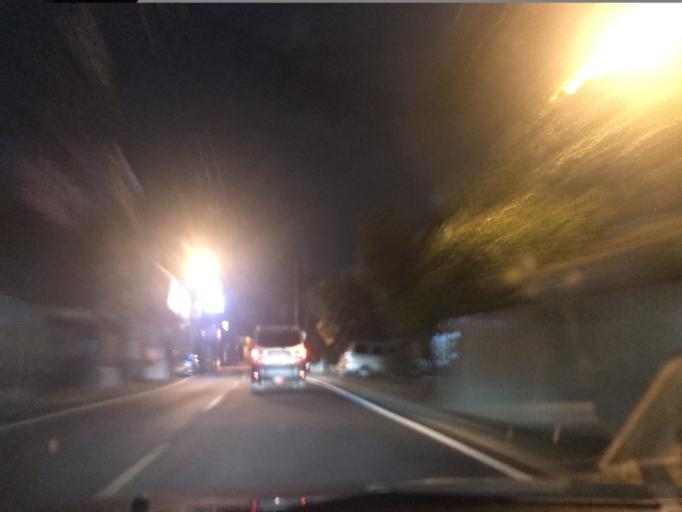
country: TW
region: Taiwan
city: Daxi
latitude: 24.9335
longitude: 121.2174
